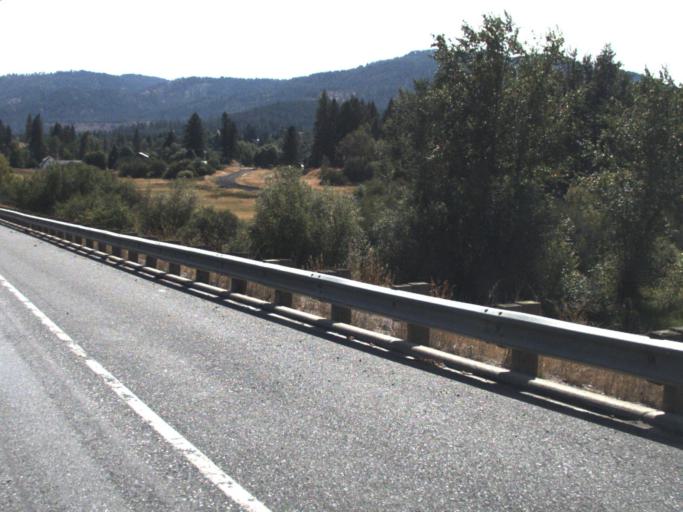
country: US
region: Washington
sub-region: Stevens County
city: Chewelah
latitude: 48.3235
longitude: -117.8230
